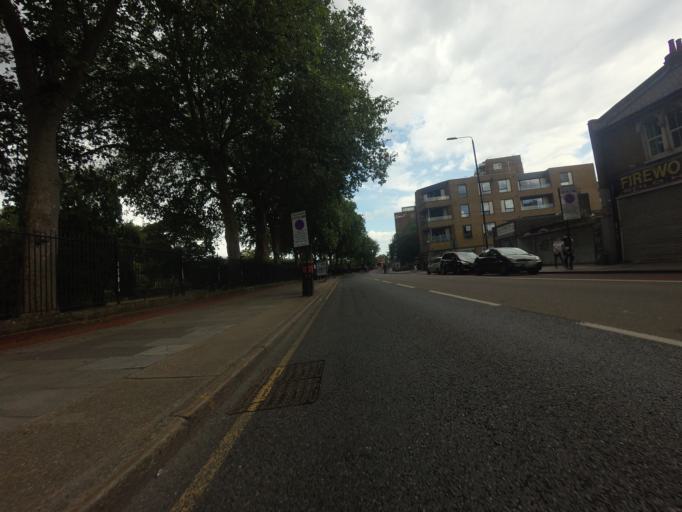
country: GB
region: England
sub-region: Greater London
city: Poplar
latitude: 51.5388
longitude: 0.0050
